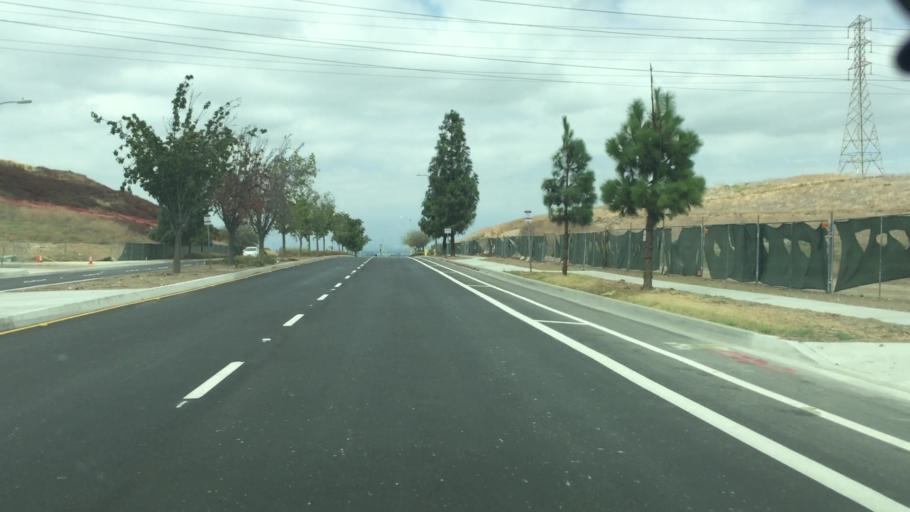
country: US
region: California
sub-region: San Bernardino County
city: Los Serranos
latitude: 33.9412
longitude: -117.6781
